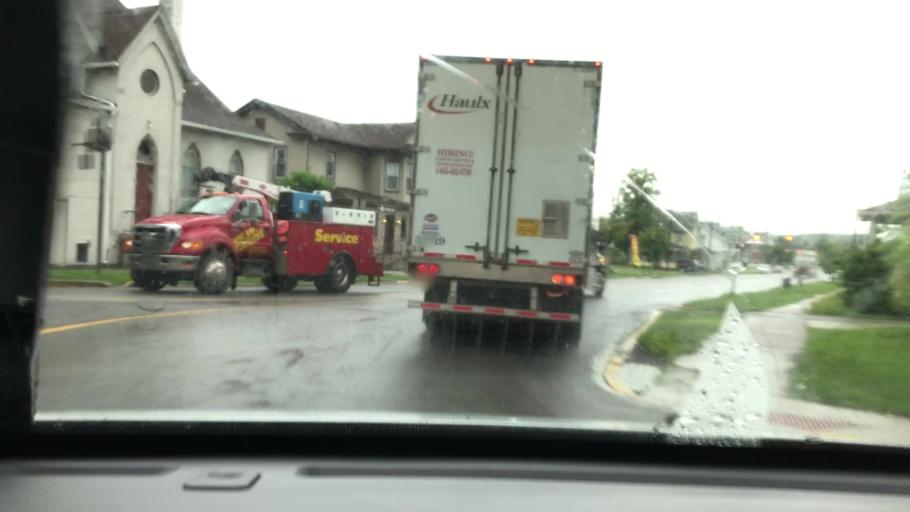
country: US
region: Pennsylvania
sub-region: Centre County
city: Philipsburg
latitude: 40.8970
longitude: -78.2208
